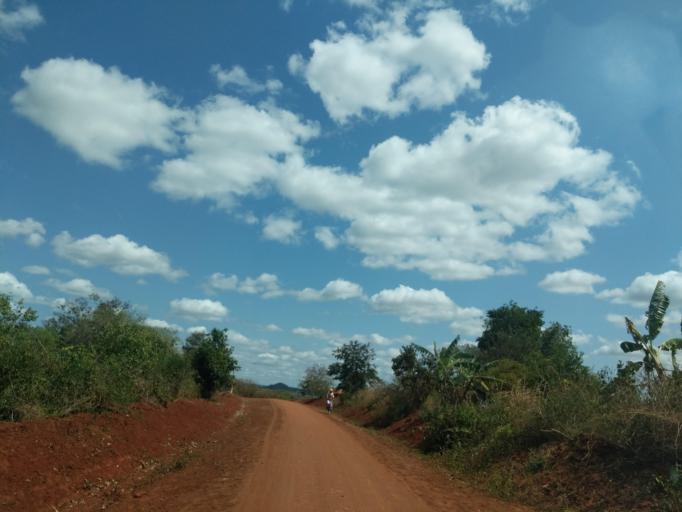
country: TZ
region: Tanga
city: Chanika
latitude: -5.5166
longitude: 38.3521
